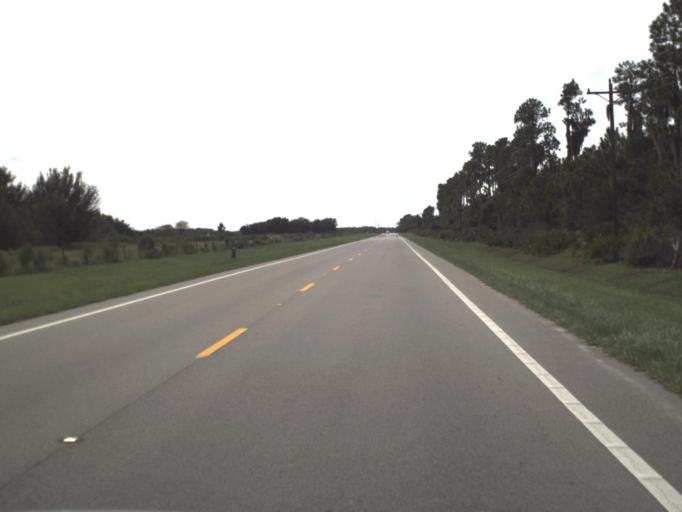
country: US
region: Florida
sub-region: Hillsborough County
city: Wimauma
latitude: 27.5860
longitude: -82.1663
